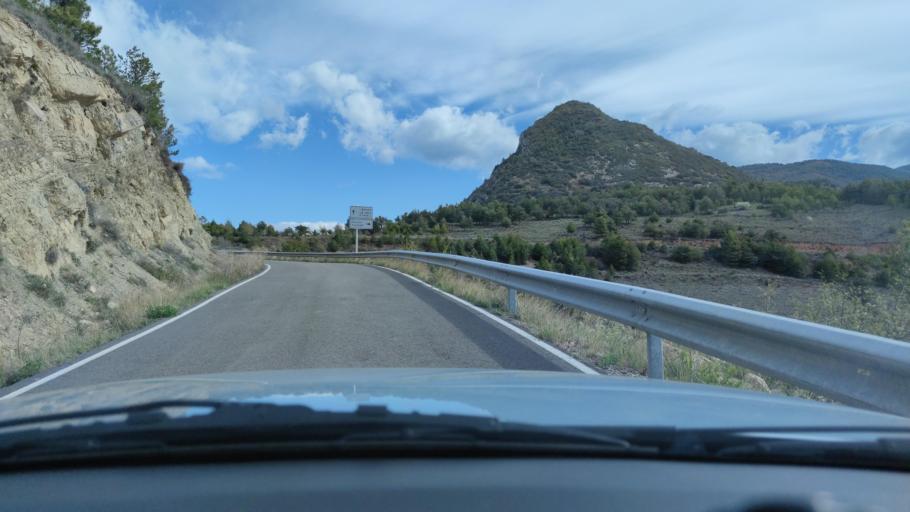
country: ES
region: Catalonia
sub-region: Provincia de Lleida
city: Alas i Cerc
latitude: 42.2520
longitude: 1.4896
